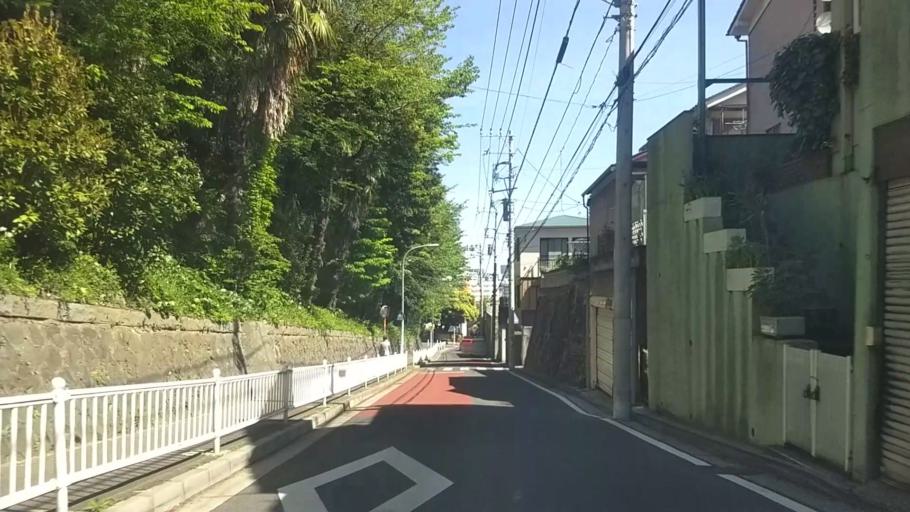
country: JP
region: Kanagawa
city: Yokohama
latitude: 35.4339
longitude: 139.6362
